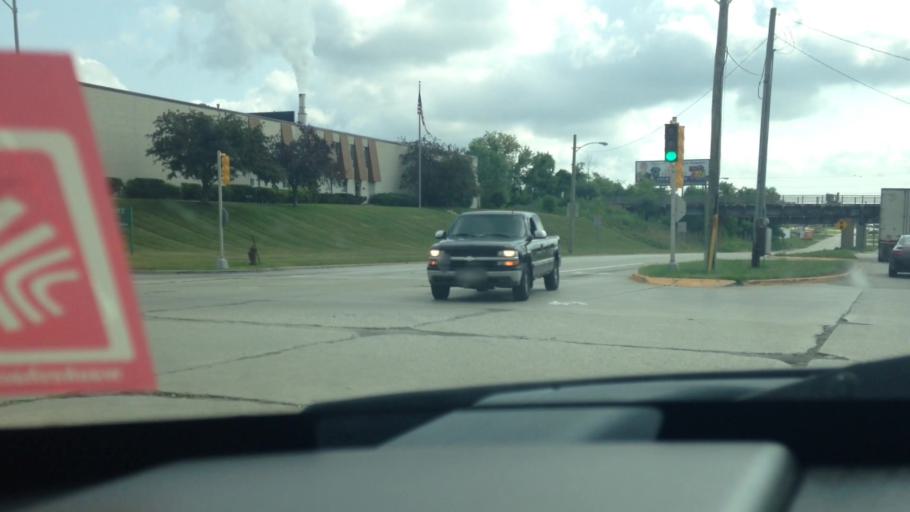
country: US
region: Wisconsin
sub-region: Waukesha County
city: Butler
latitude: 43.1169
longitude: -88.0657
